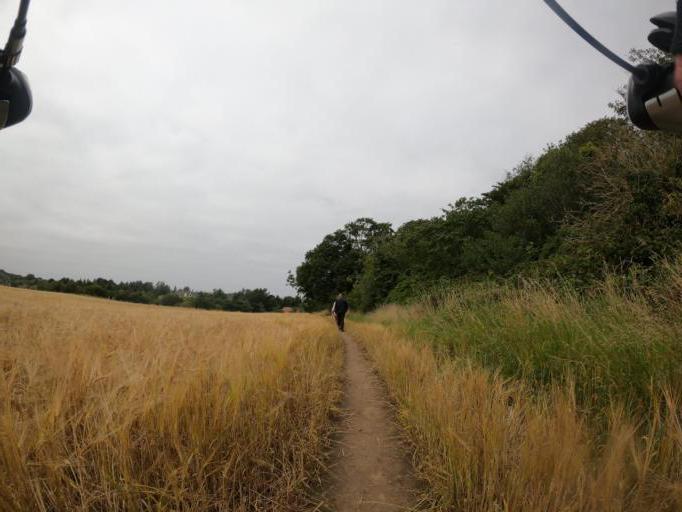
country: GB
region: Scotland
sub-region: East Lothian
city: Musselburgh
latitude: 55.9438
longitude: -3.0820
